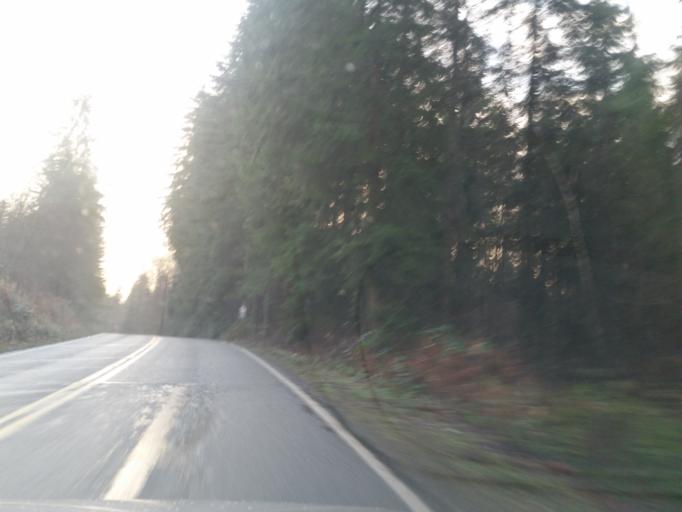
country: US
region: Washington
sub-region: Snohomish County
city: Maltby
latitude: 47.8127
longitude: -122.0971
